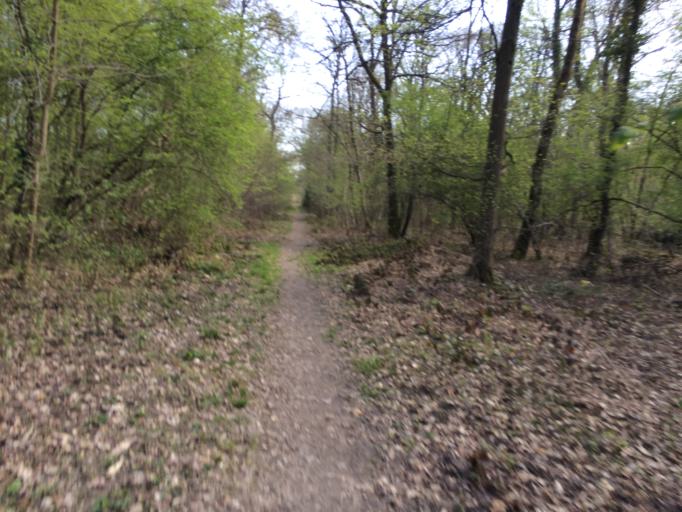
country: FR
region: Ile-de-France
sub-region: Departement de l'Essonne
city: Draveil
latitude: 48.6699
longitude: 2.4202
